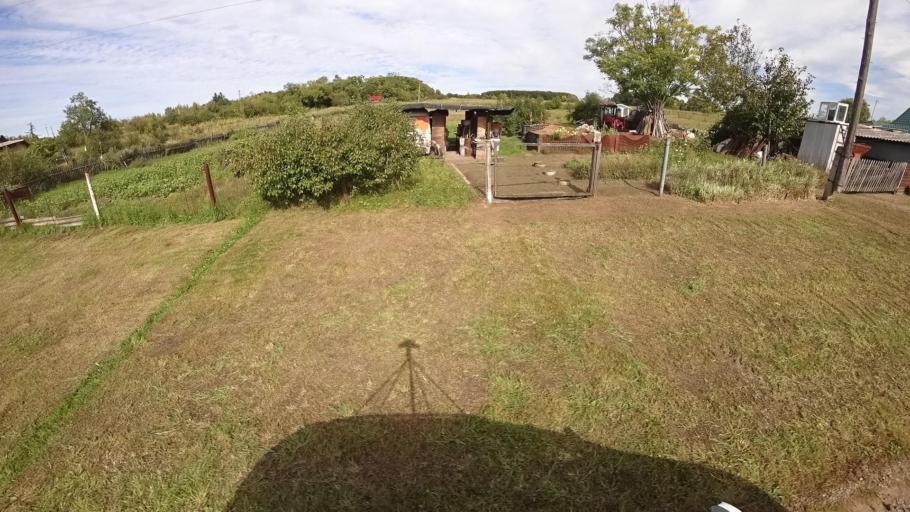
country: RU
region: Primorskiy
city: Dostoyevka
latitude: 44.3192
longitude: 133.4774
